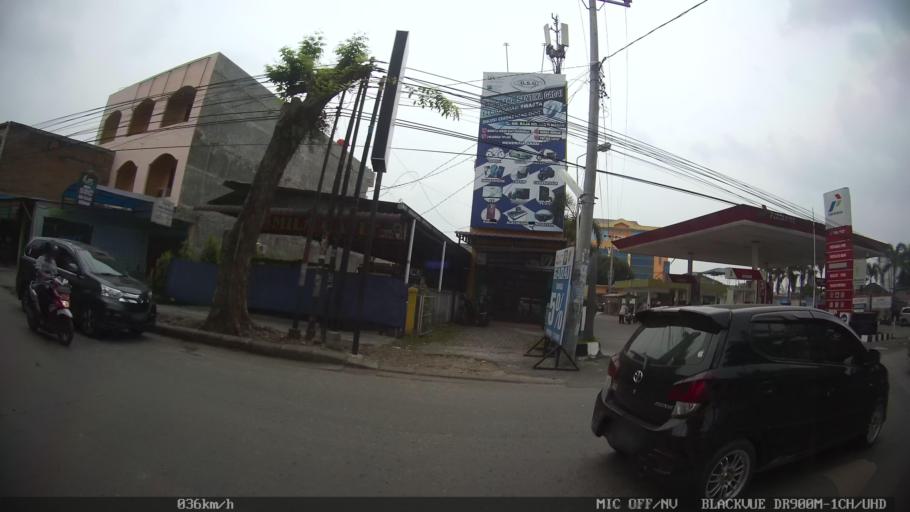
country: ID
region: North Sumatra
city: Medan
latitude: 3.5583
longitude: 98.6944
